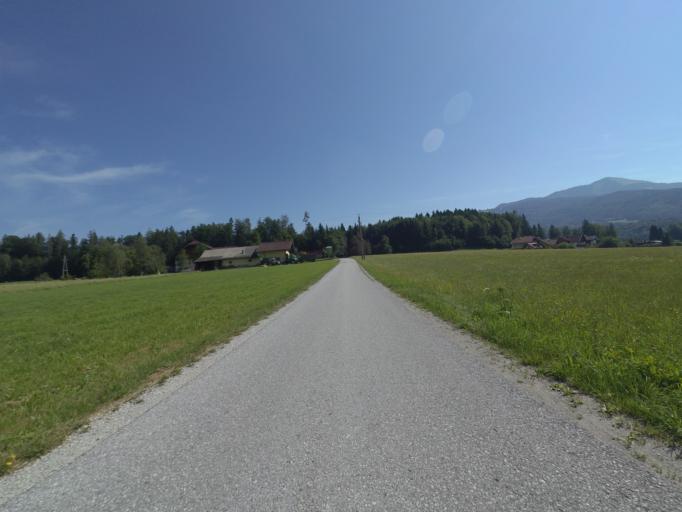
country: AT
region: Salzburg
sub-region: Politischer Bezirk Hallein
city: Adnet
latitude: 47.6805
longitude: 13.1313
